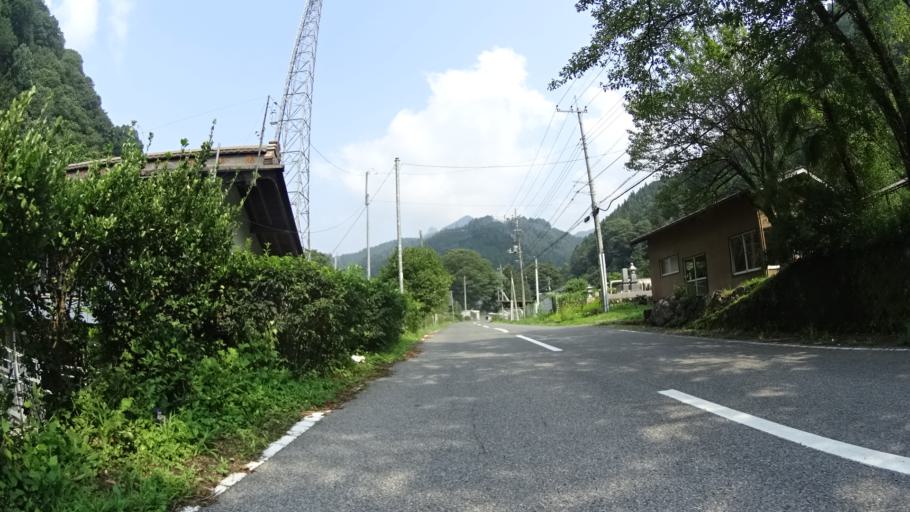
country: JP
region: Saitama
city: Chichibu
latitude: 36.0463
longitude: 138.8892
